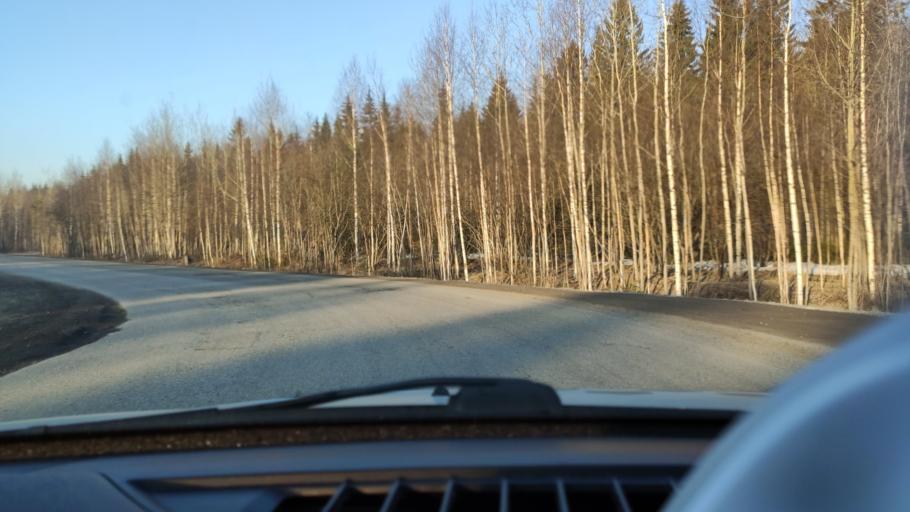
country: RU
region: Perm
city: Polazna
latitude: 58.1139
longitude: 56.4254
